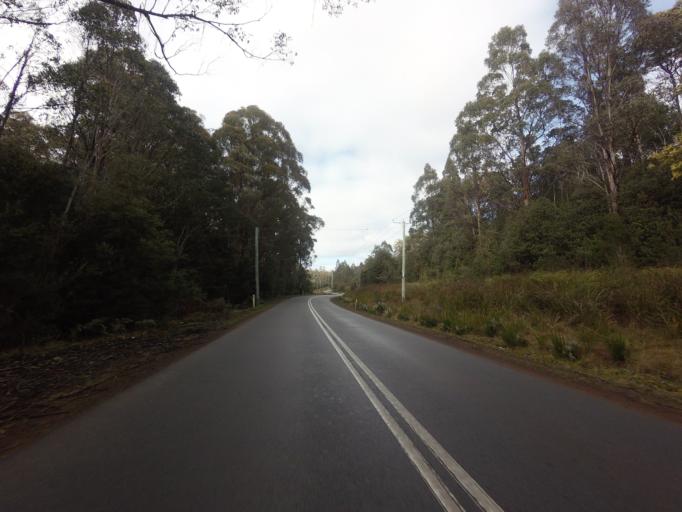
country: AU
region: Tasmania
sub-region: Huon Valley
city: Geeveston
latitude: -43.3640
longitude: 146.9592
